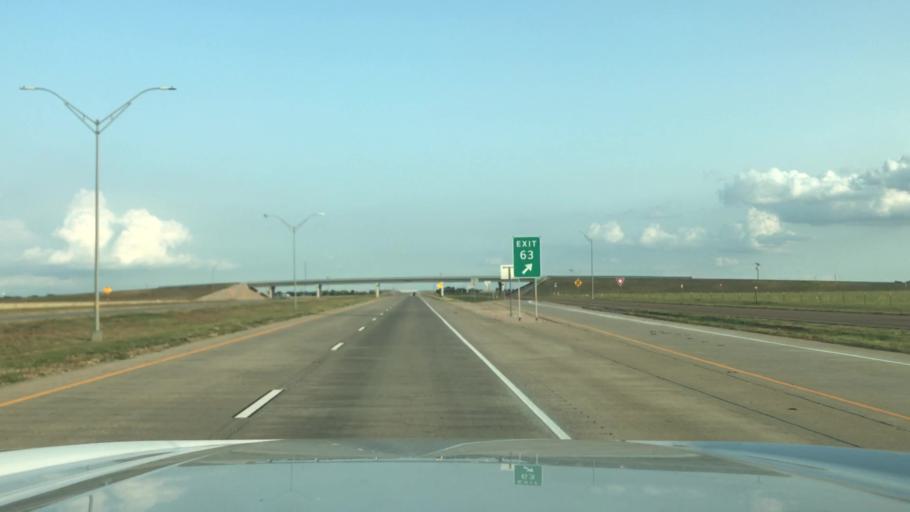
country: US
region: Texas
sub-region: Swisher County
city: Tulia
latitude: 34.3718
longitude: -101.7689
